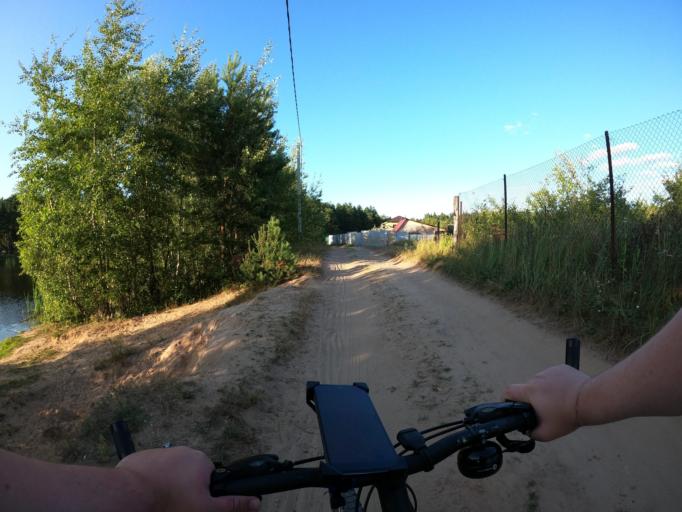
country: RU
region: Moskovskaya
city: Beloozerskiy
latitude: 55.4939
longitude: 38.4375
